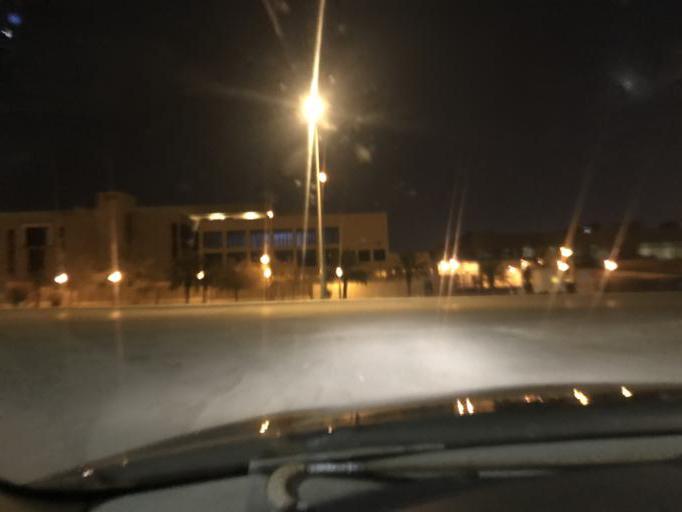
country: SA
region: Ar Riyad
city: Riyadh
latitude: 24.8125
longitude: 46.6900
